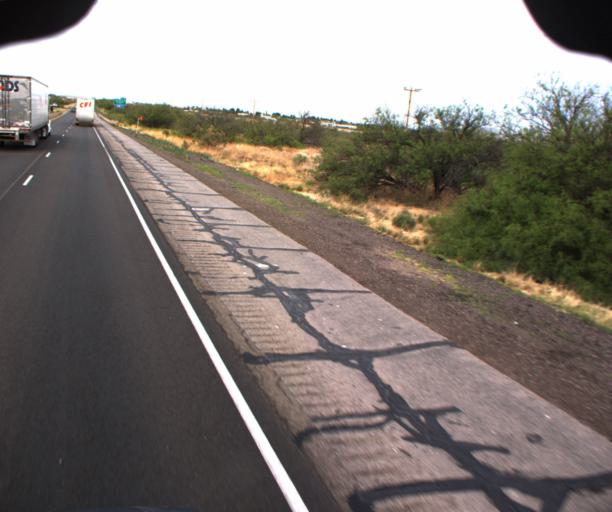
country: US
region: Arizona
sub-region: Cochise County
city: Mescal
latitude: 31.9632
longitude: -110.4174
